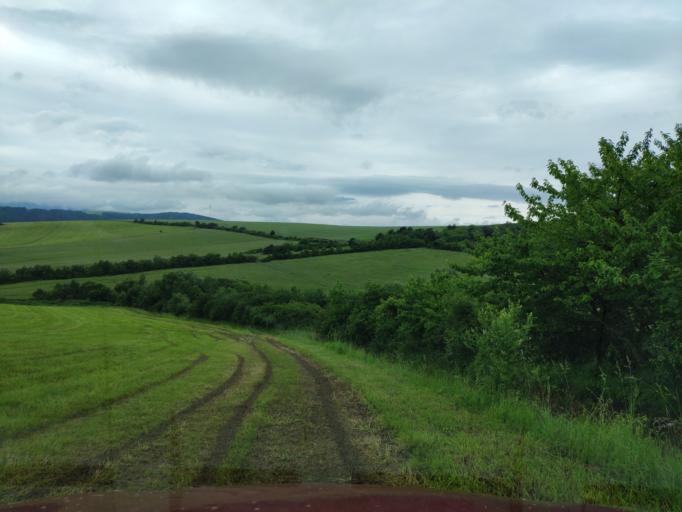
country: SK
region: Presovsky
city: Sabinov
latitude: 49.0527
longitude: 21.0086
